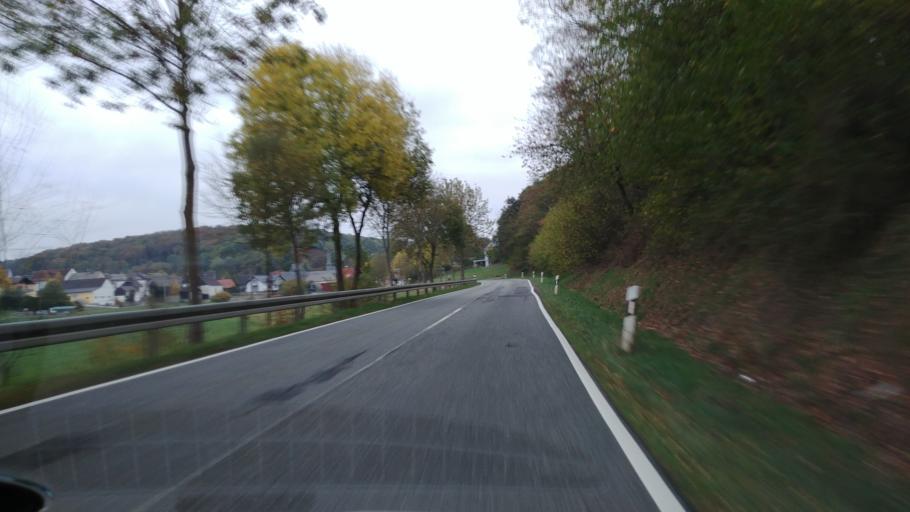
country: DE
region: Rheinland-Pfalz
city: Kaltenholzhausen
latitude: 50.2626
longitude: 8.1470
